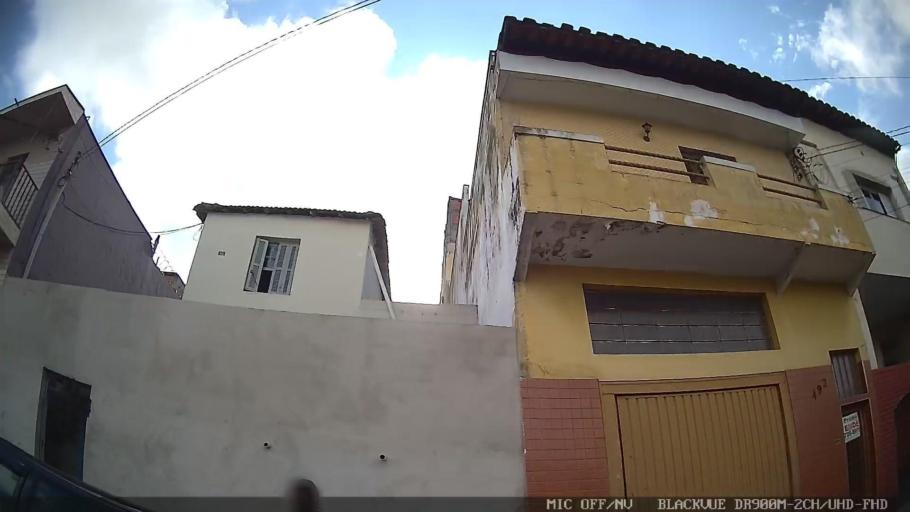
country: BR
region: Sao Paulo
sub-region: Sao Caetano Do Sul
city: Sao Caetano do Sul
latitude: -23.5660
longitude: -46.5368
